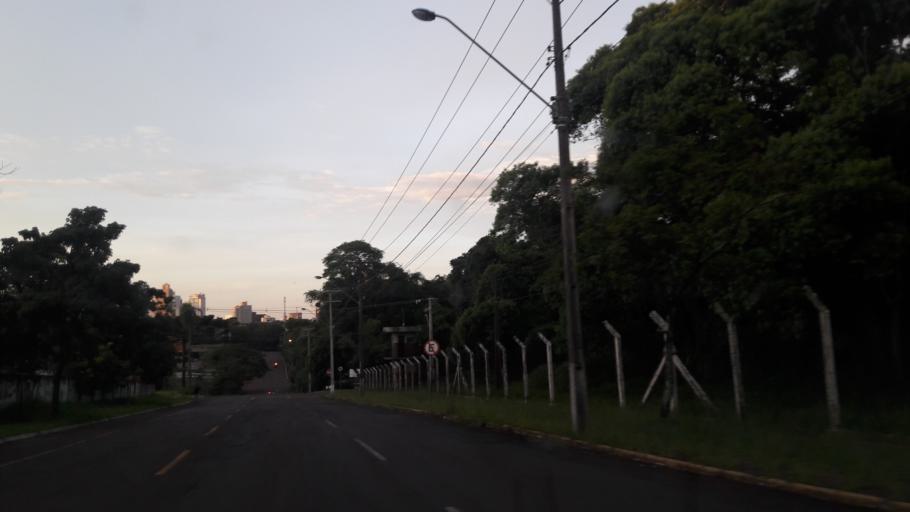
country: BR
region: Parana
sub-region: Cascavel
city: Cascavel
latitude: -24.9604
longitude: -53.4500
